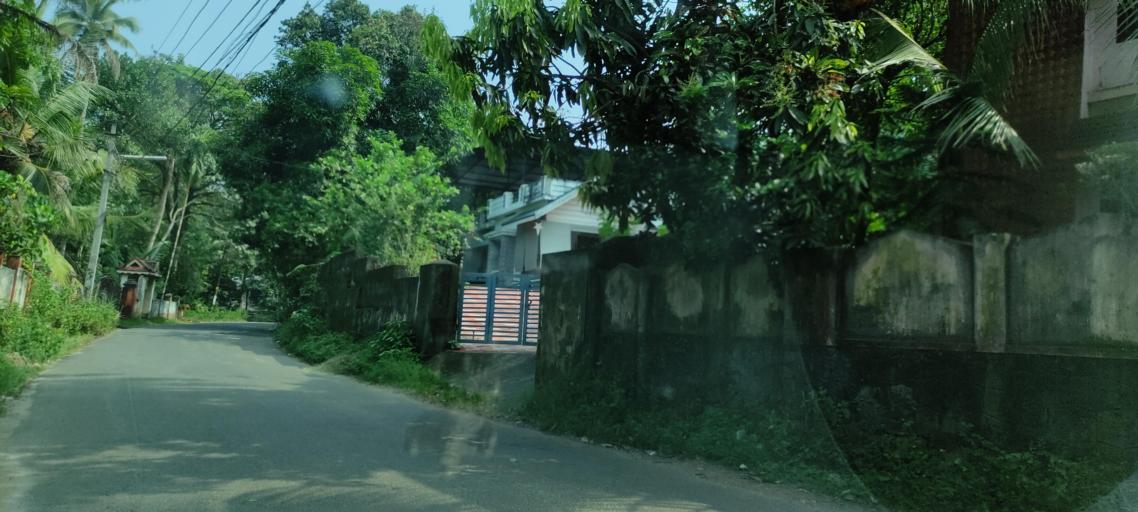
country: IN
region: Kerala
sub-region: Pattanamtitta
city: Adur
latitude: 9.2253
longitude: 76.7130
